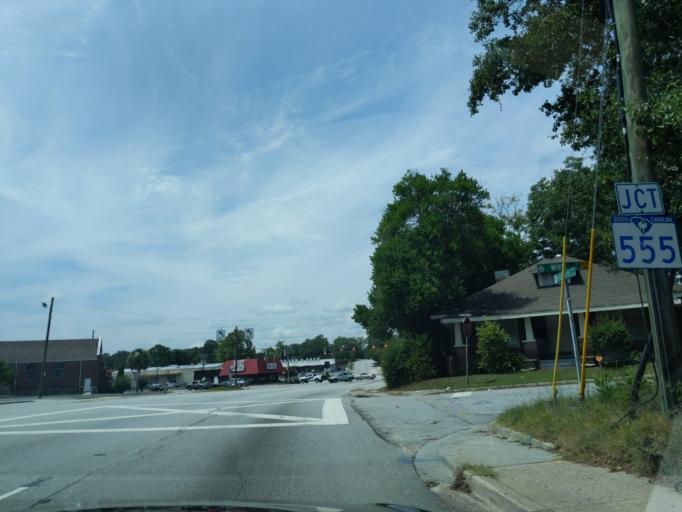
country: US
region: South Carolina
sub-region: Richland County
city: Columbia
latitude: 34.0326
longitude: -81.0224
